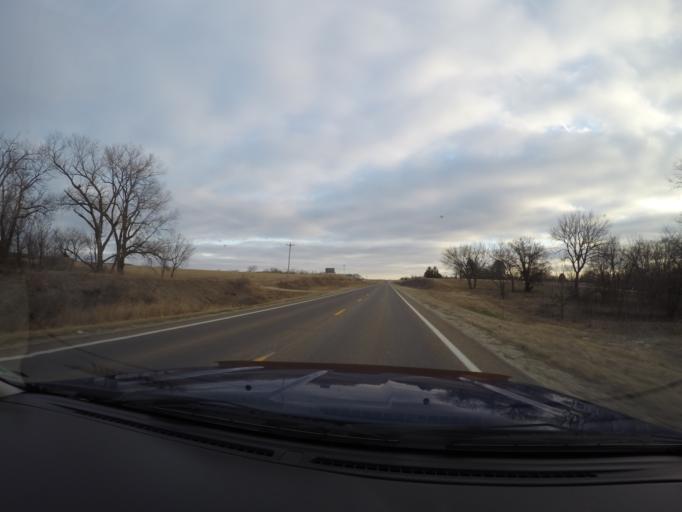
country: US
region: Kansas
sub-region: Morris County
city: Council Grove
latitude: 38.6942
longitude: -96.4947
